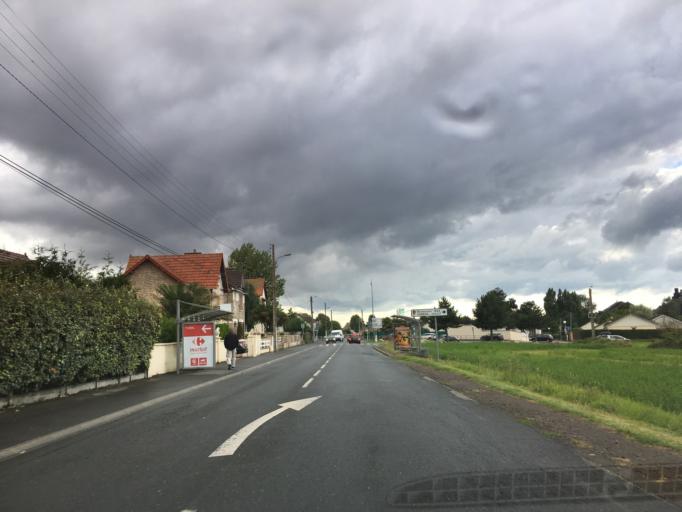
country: FR
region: Lower Normandy
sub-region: Departement du Calvados
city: Courseulles-sur-Mer
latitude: 49.3301
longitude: -0.4453
